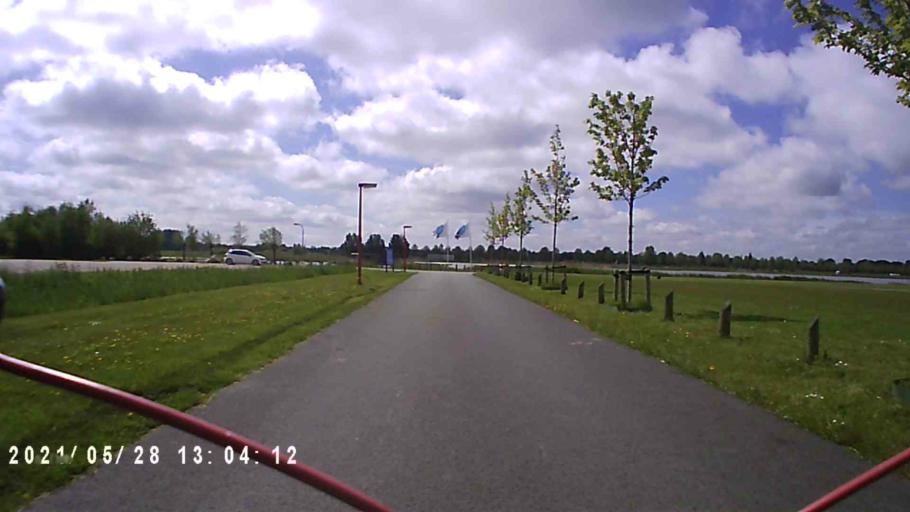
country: NL
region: Groningen
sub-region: Gemeente  Oldambt
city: Winschoten
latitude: 53.1646
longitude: 7.0388
